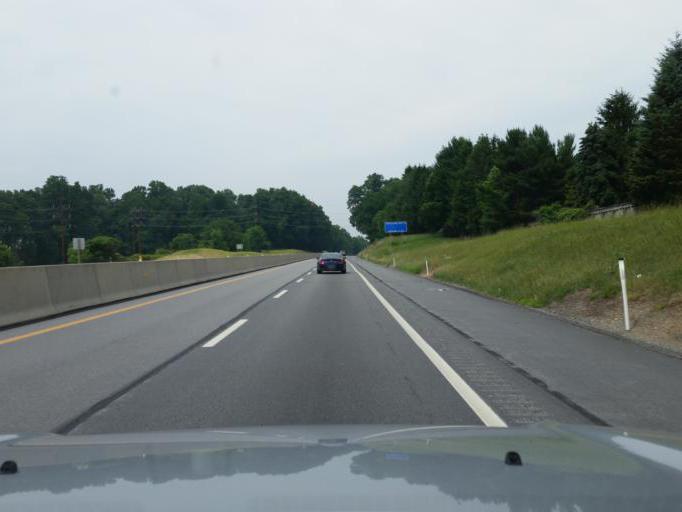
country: US
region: Pennsylvania
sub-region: Cumberland County
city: Shiremanstown
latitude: 40.1981
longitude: -76.9555
